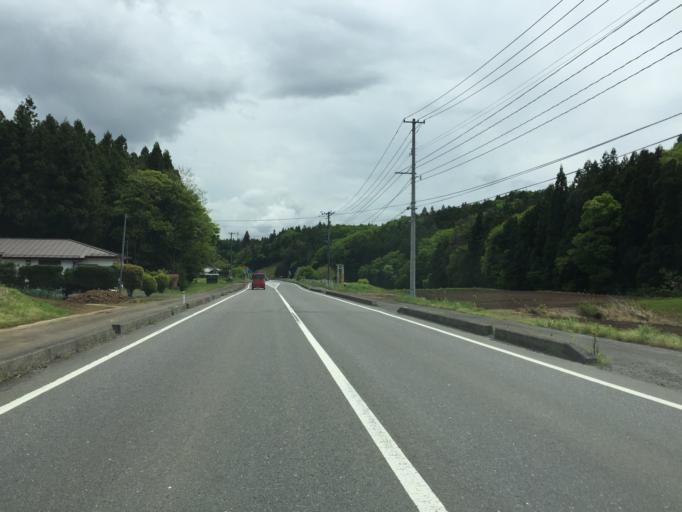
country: JP
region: Fukushima
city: Ishikawa
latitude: 37.0732
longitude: 140.3622
